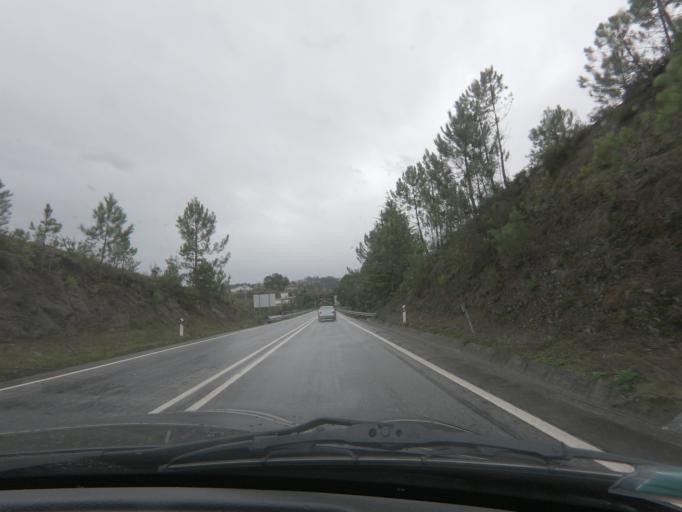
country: PT
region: Porto
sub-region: Amarante
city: Teloes
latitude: 41.3225
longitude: -8.0636
